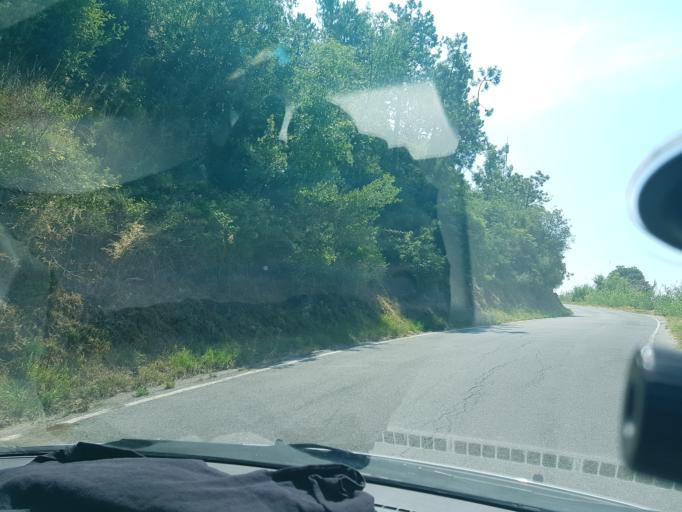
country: IT
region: Liguria
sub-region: Provincia di Genova
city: San Teodoro
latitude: 44.4365
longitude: 8.8414
